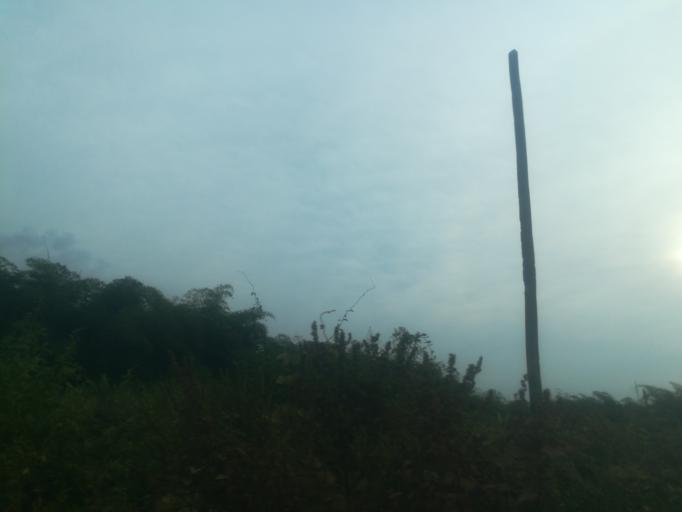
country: NG
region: Ogun
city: Ayetoro
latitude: 7.2140
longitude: 3.1835
